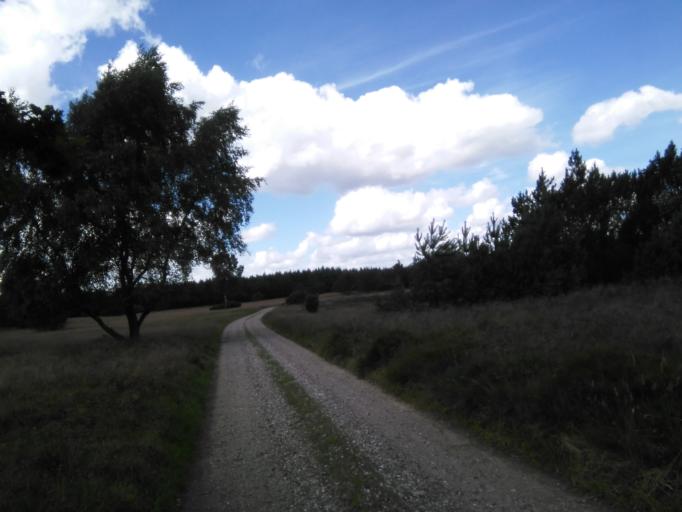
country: DK
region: Central Jutland
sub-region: Silkeborg Kommune
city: Virklund
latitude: 56.0867
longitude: 9.4336
